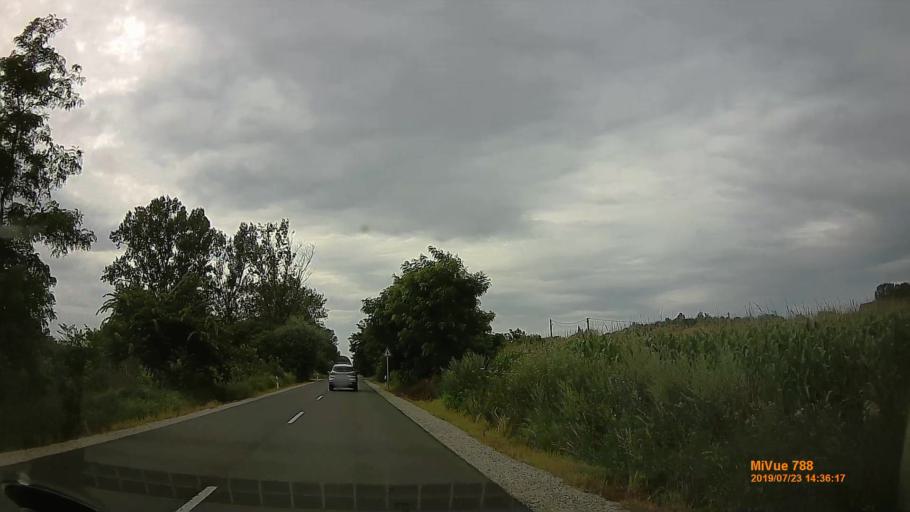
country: HU
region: Szabolcs-Szatmar-Bereg
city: Nyiregyhaza
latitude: 47.9318
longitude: 21.7021
